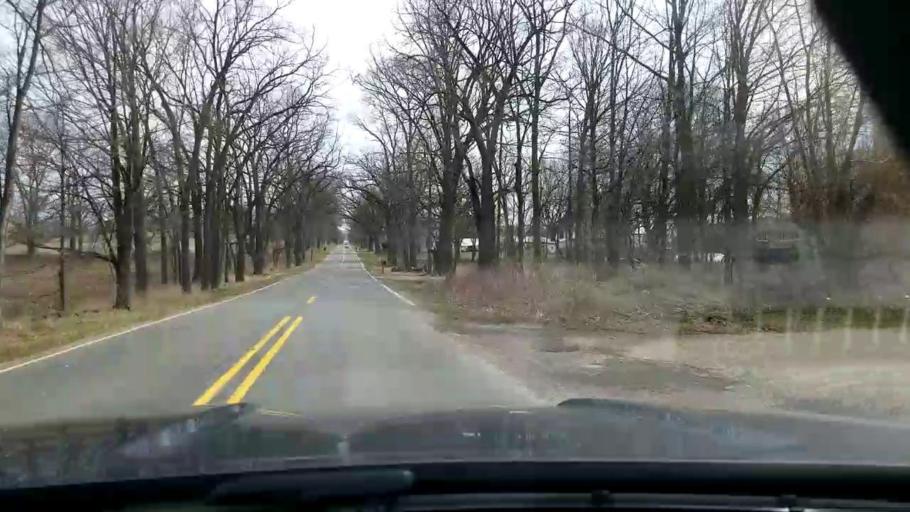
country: US
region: Michigan
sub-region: Jackson County
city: Spring Arbor
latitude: 42.1014
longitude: -84.5163
